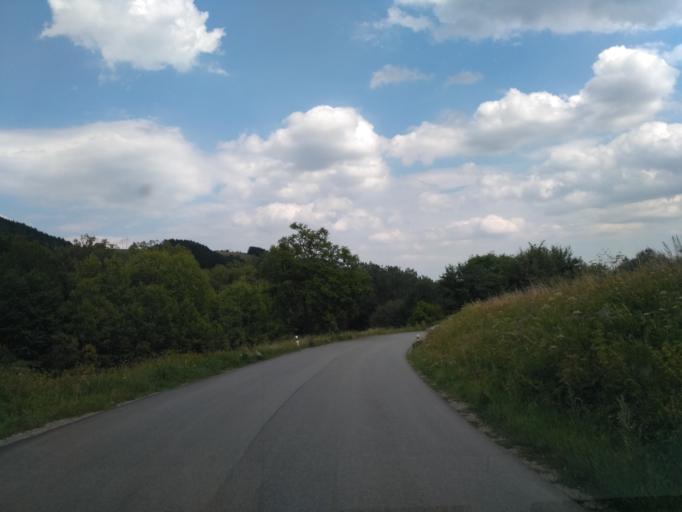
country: SK
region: Kosicky
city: Gelnica
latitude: 48.9231
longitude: 21.0625
